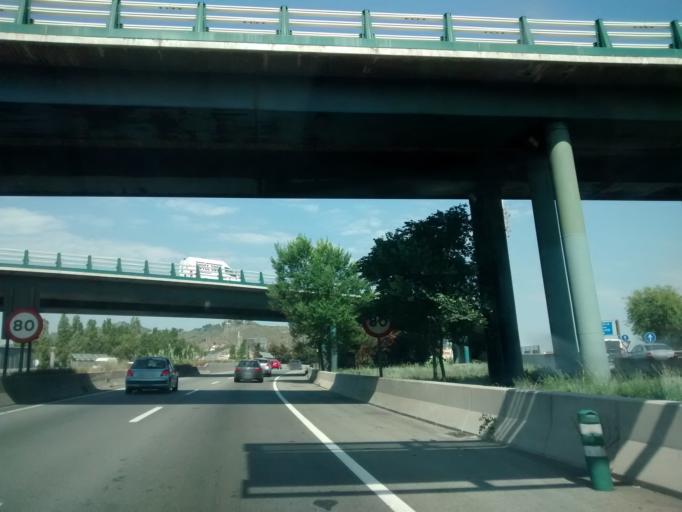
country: ES
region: Catalonia
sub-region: Provincia de Barcelona
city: Santa Coloma de Gramenet
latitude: 41.4495
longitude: 2.1985
